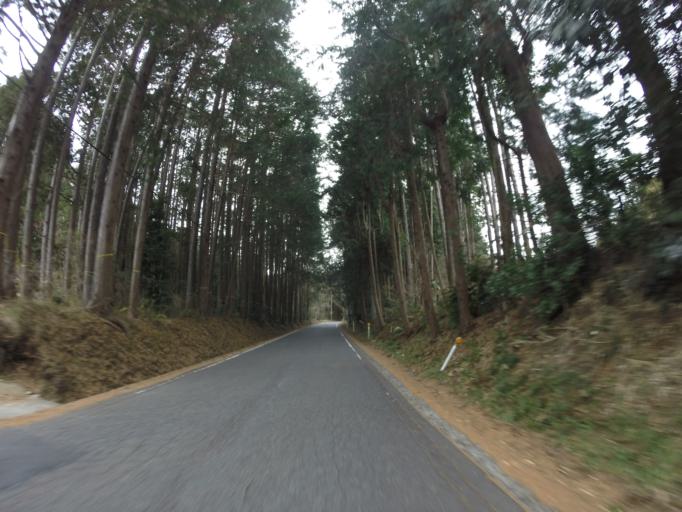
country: JP
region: Shizuoka
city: Fujinomiya
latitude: 35.2362
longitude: 138.5778
